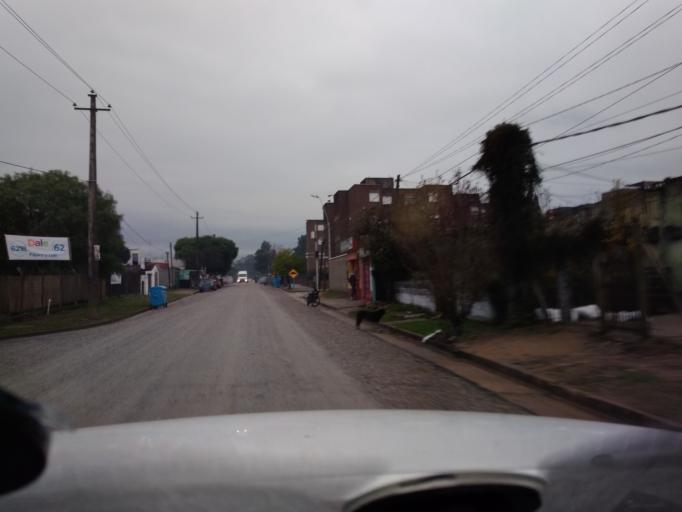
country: UY
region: Florida
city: Florida
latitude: -34.1075
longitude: -56.2105
